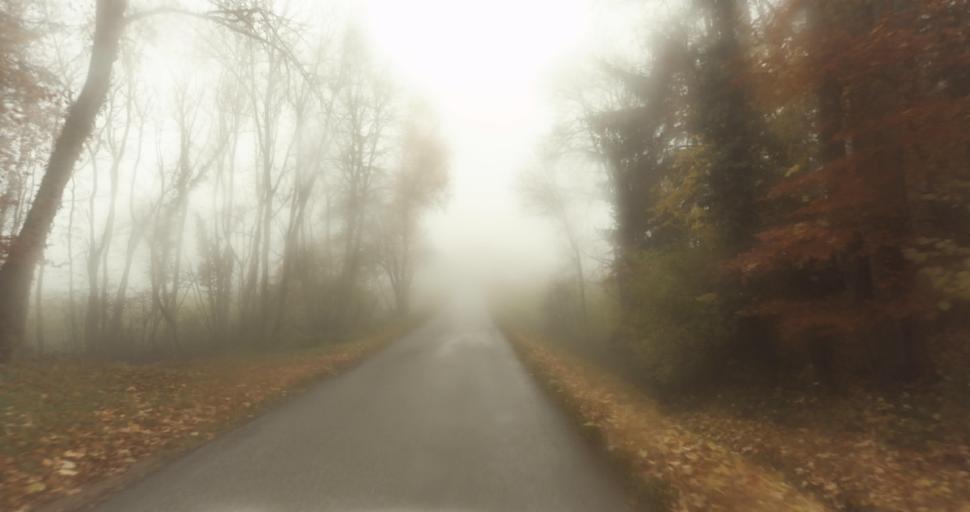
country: FR
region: Rhone-Alpes
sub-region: Departement de la Haute-Savoie
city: Villaz
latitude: 45.9796
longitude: 6.2061
